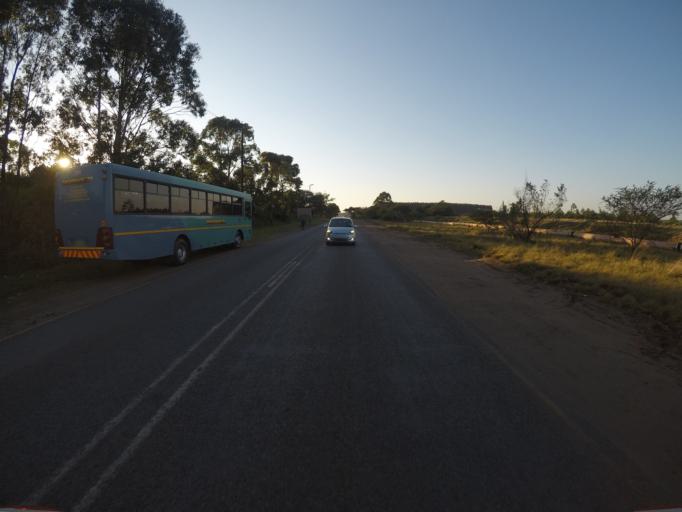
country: ZA
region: KwaZulu-Natal
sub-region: uThungulu District Municipality
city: KwaMbonambi
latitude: -28.6873
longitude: 32.1424
